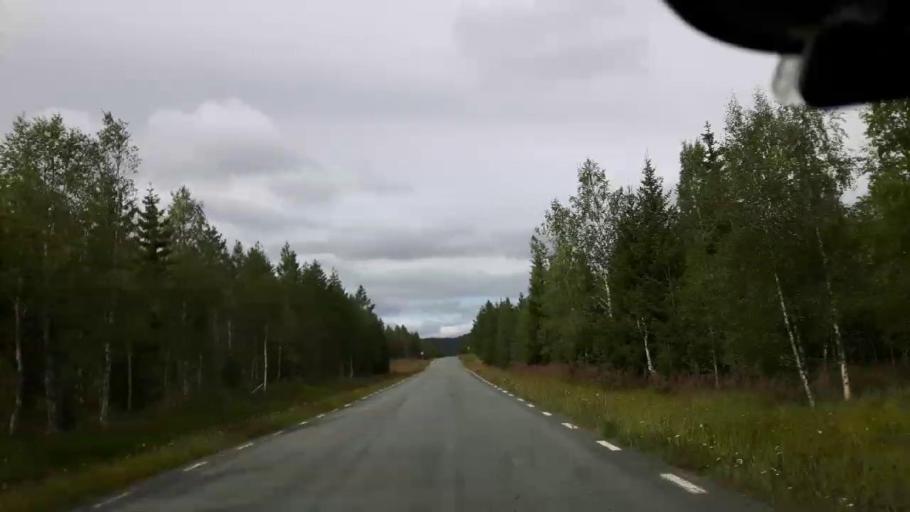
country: SE
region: Jaemtland
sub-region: Krokoms Kommun
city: Valla
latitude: 63.4752
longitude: 13.9968
